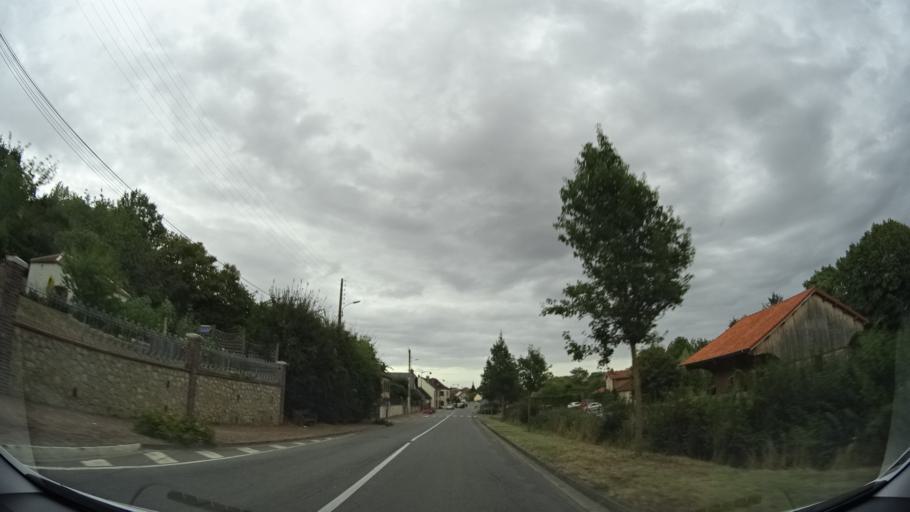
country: FR
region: Centre
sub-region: Departement du Loiret
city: Saint-Germain-des-Pres
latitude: 47.9531
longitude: 2.8396
